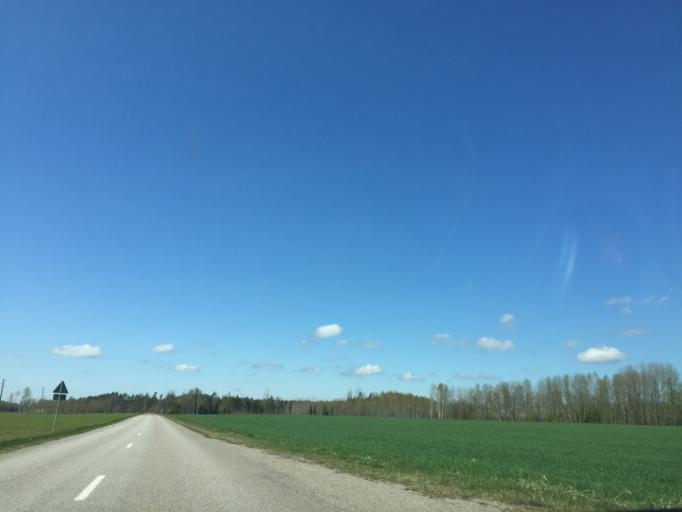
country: LV
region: Strenci
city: Seda
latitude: 57.5675
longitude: 25.8104
